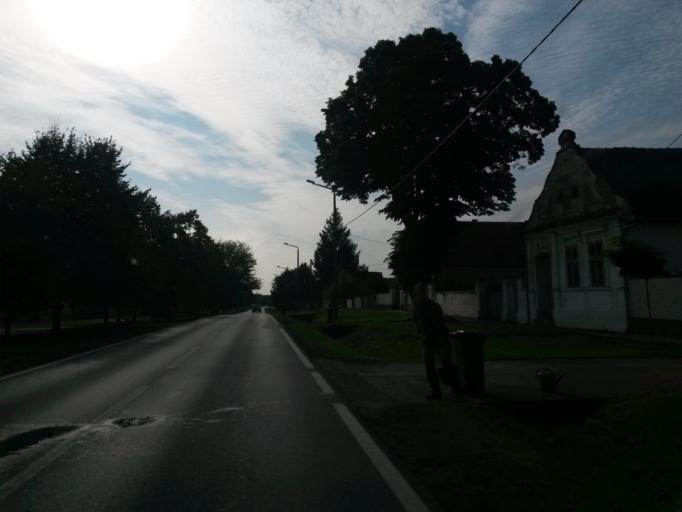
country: HR
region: Vukovarsko-Srijemska
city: Lovas
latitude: 45.2913
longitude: 19.1011
